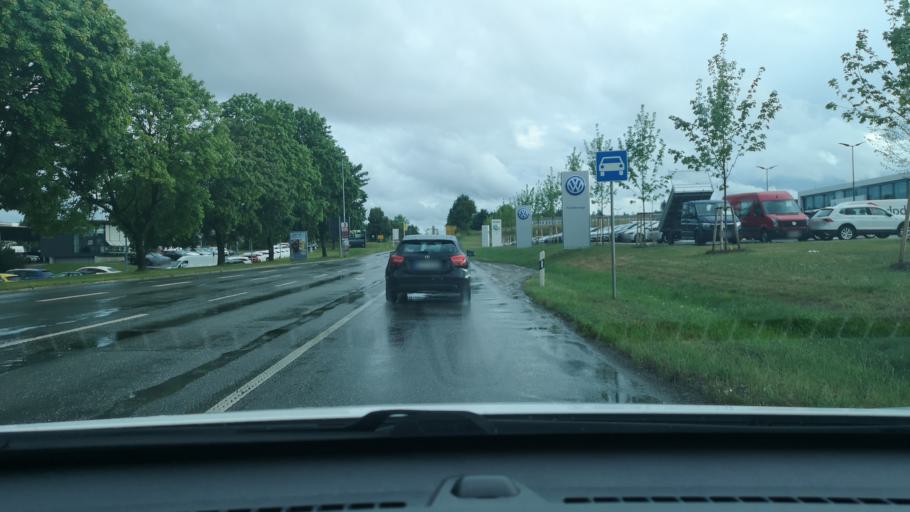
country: DE
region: Baden-Wuerttemberg
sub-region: Freiburg Region
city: Rottweil
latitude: 48.1475
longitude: 8.6404
